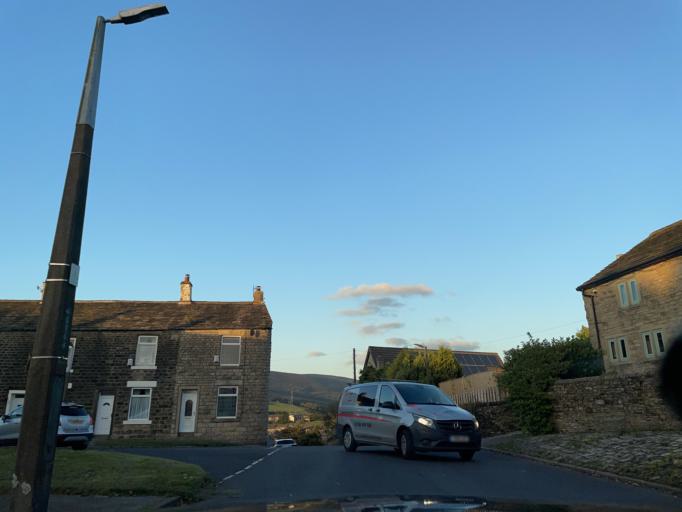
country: GB
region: England
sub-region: Derbyshire
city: Glossop
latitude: 53.4619
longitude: -1.9699
